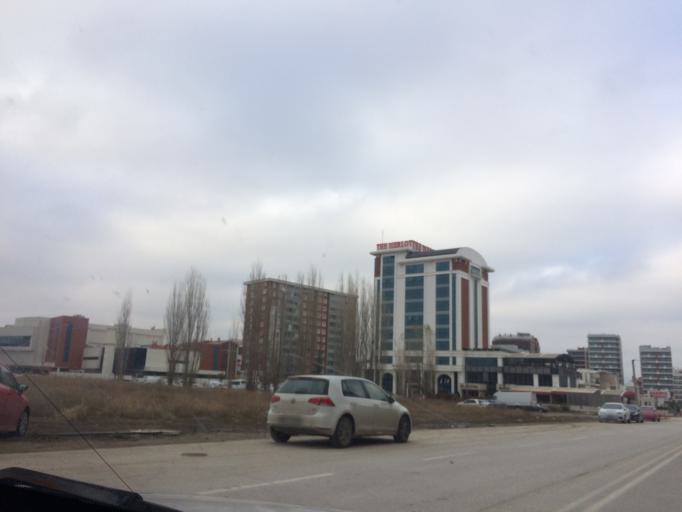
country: TR
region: Eskisehir
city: Eskisehir
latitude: 39.7816
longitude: 30.4987
